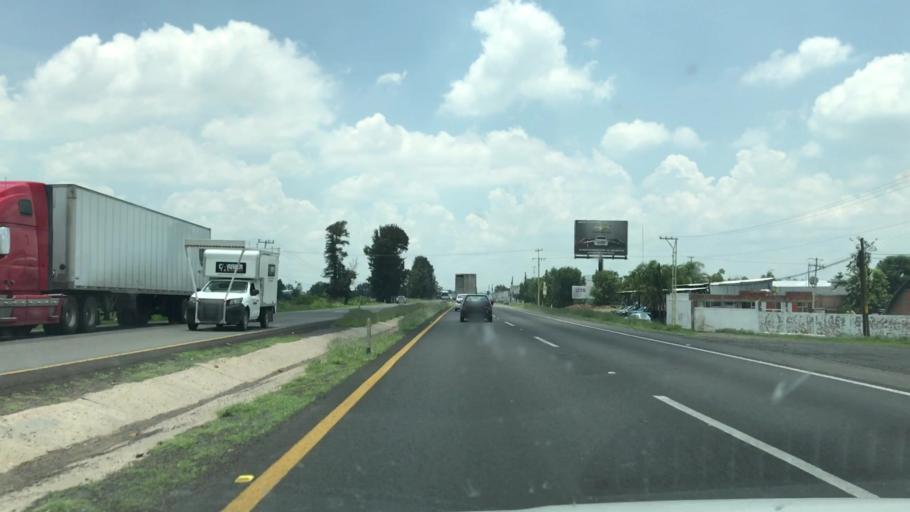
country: MX
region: Guanajuato
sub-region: Irapuato
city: San Jose de Bernalejo (El Guayabo)
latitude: 20.6144
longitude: -101.4052
